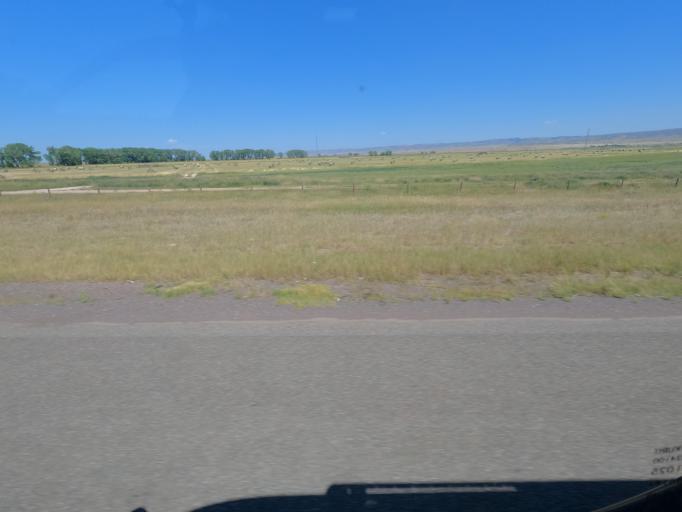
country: US
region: Wyoming
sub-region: Albany County
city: Laramie
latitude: 41.3443
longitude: -105.6264
